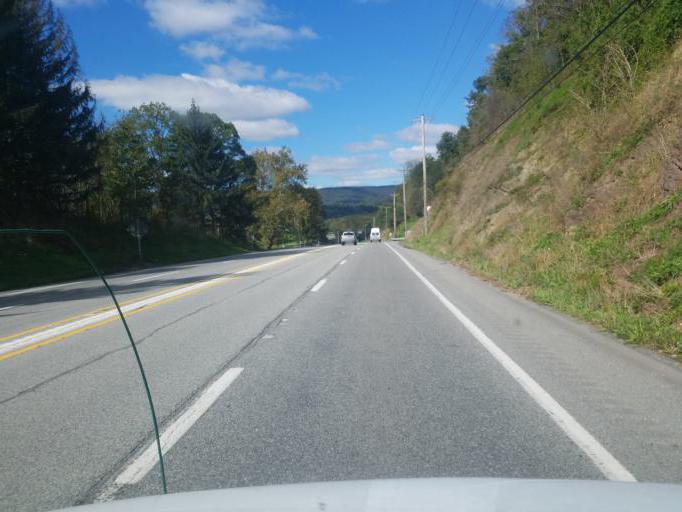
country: US
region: Pennsylvania
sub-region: Bedford County
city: Earlston
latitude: 40.0181
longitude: -78.3279
